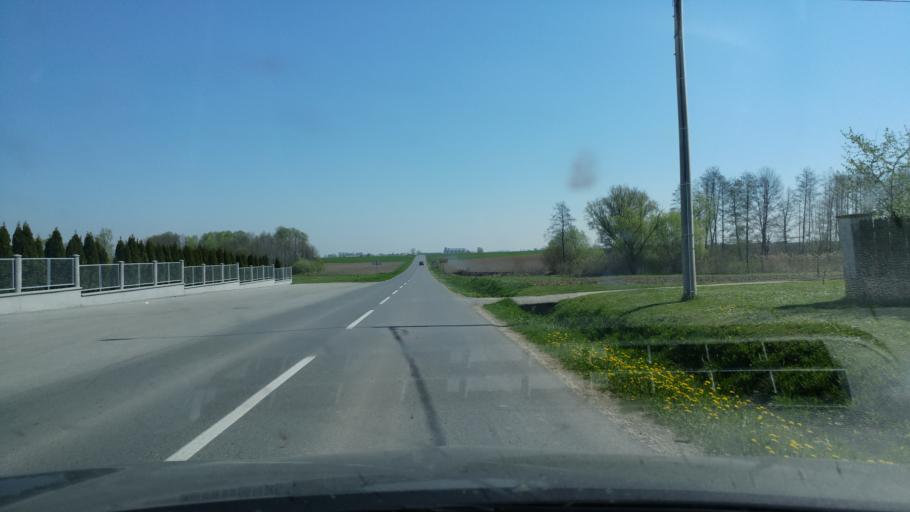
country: HR
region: Osjecko-Baranjska
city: Viskovci
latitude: 45.3507
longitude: 18.5021
